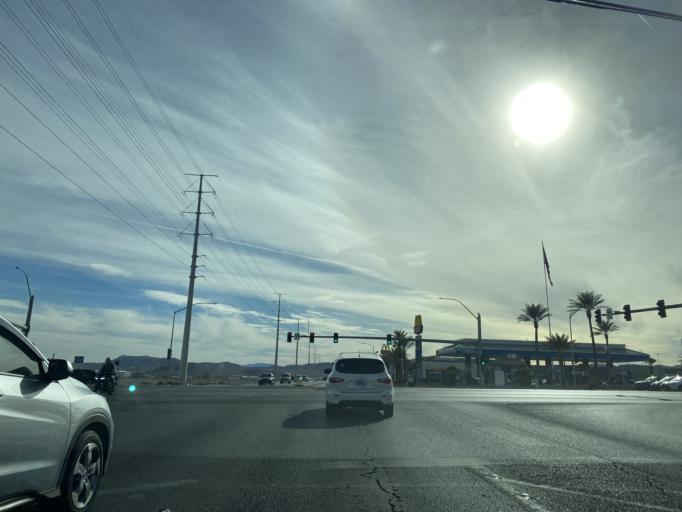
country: US
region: Nevada
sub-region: Clark County
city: Enterprise
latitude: 36.0228
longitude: -115.2436
